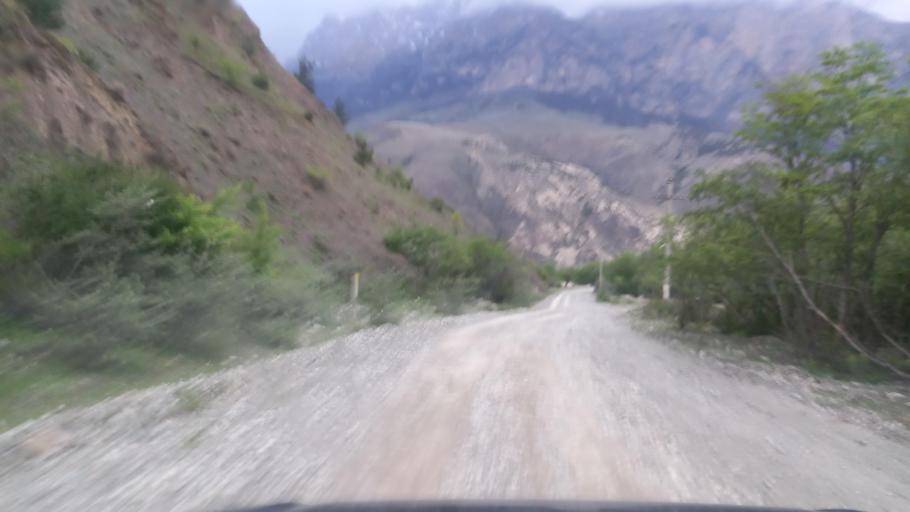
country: RU
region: North Ossetia
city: Mizur
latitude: 42.8532
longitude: 44.1531
